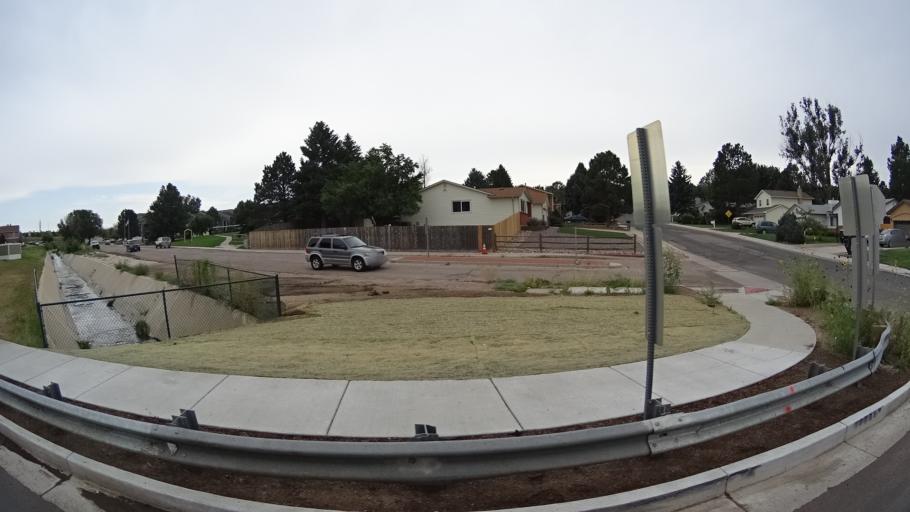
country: US
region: Colorado
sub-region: El Paso County
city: Colorado Springs
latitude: 38.9244
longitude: -104.7973
